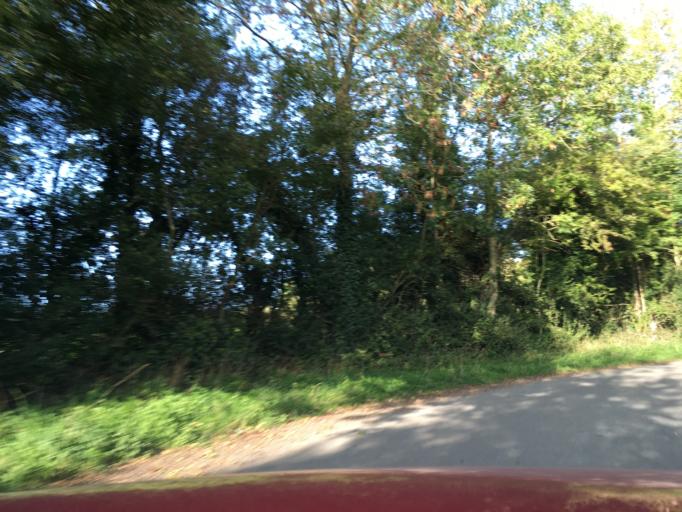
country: GB
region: England
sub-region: Gloucestershire
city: Newent
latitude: 51.9659
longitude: -2.3108
